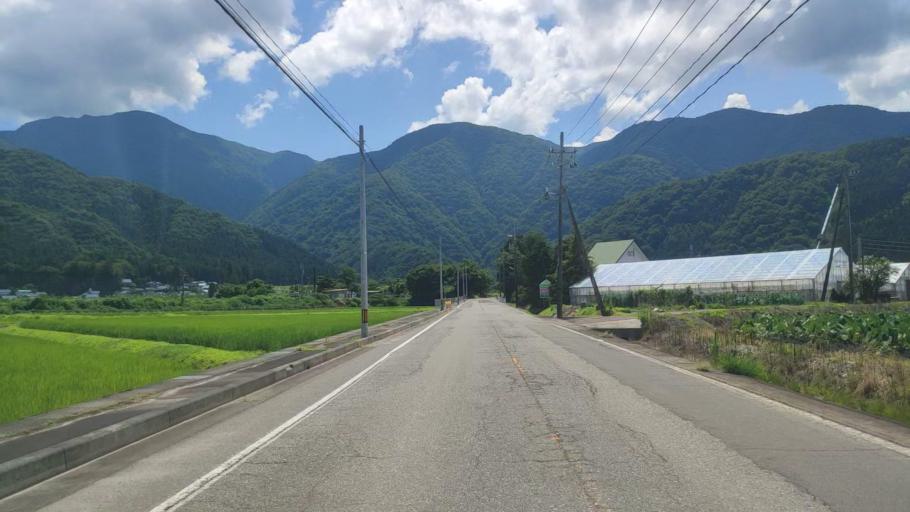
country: JP
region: Fukui
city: Ono
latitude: 35.9422
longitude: 136.5479
